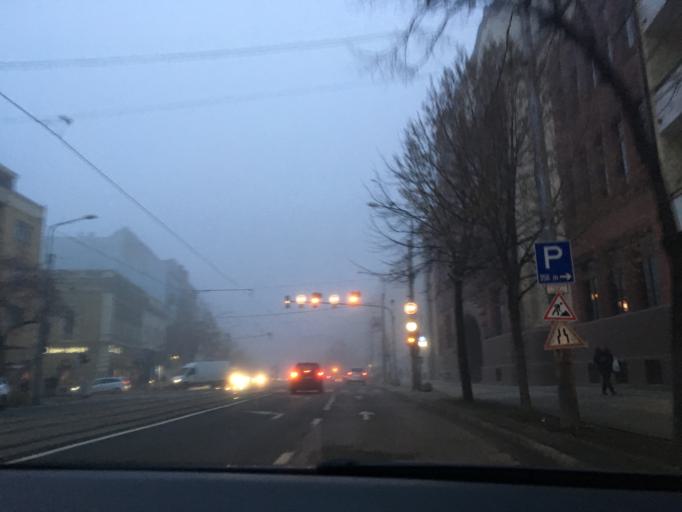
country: HU
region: Hajdu-Bihar
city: Debrecen
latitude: 47.5256
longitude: 21.6266
